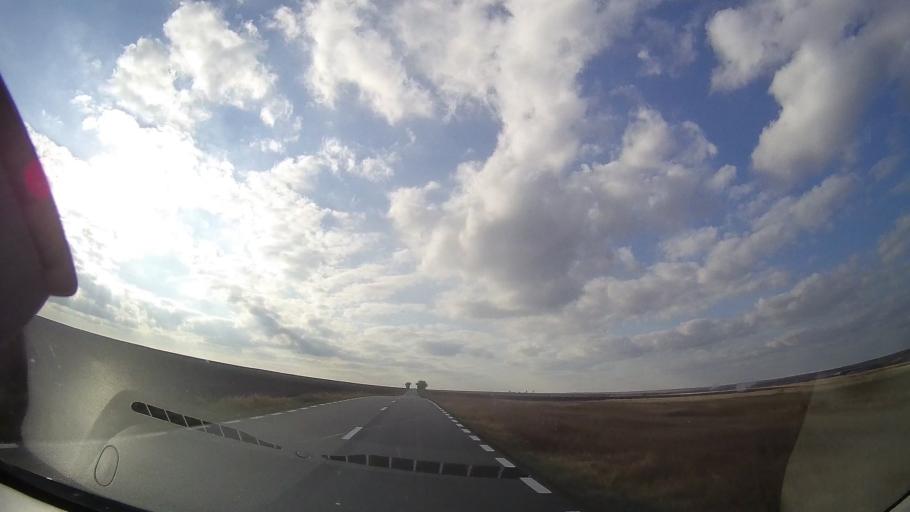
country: RO
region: Constanta
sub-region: Comuna Albesti
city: Albesti
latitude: 43.8080
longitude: 28.3980
